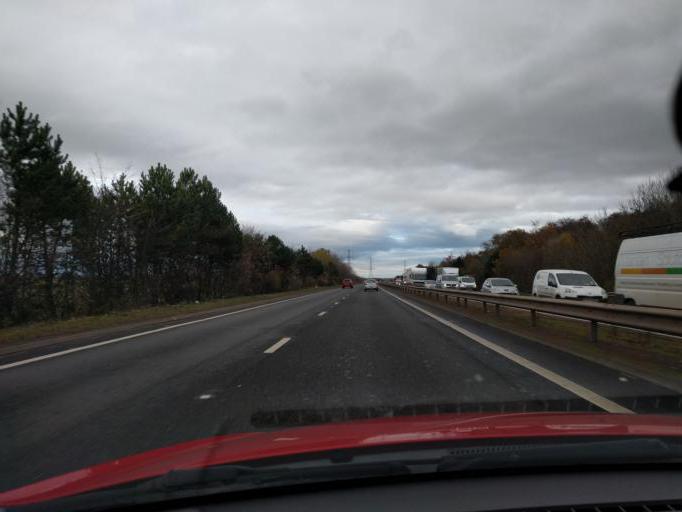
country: GB
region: Scotland
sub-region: Midlothian
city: Dalkeith
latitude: 55.9041
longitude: -3.0829
